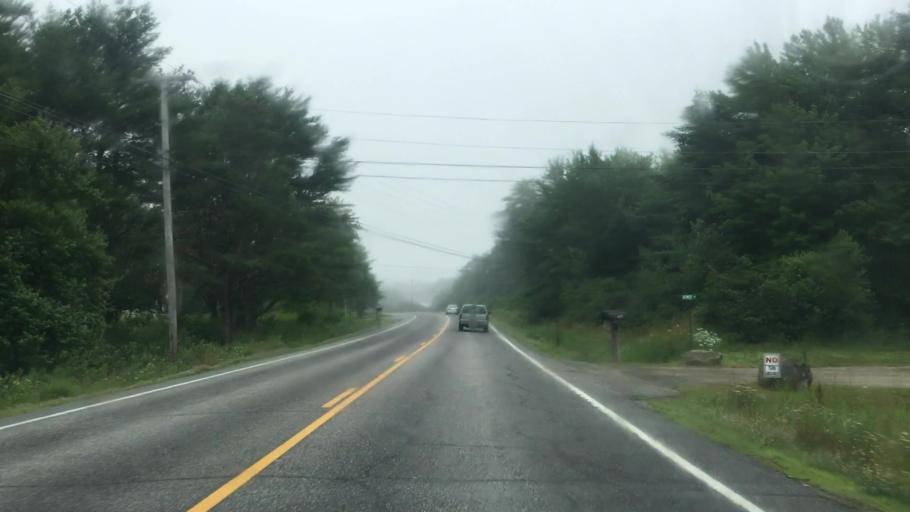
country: US
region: Maine
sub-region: Lincoln County
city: Edgecomb
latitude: 43.9452
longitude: -69.6279
